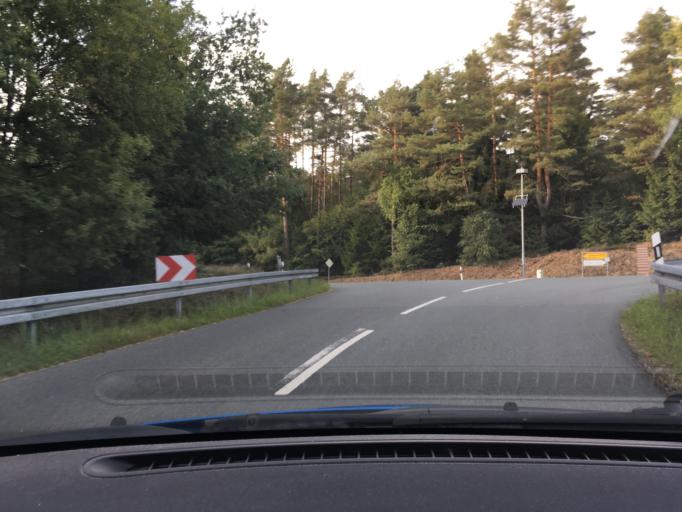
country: DE
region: Lower Saxony
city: Fassberg
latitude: 52.9078
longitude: 10.0936
